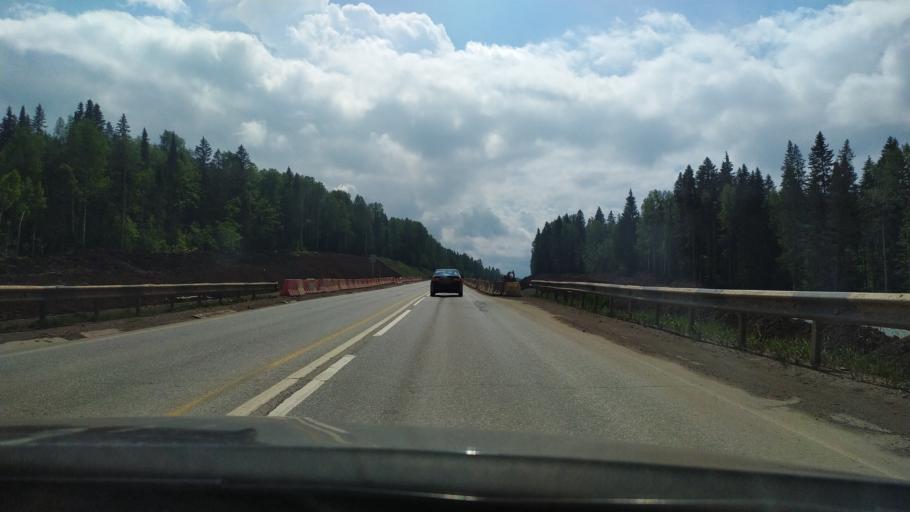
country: RU
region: Perm
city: Novyye Lyady
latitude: 58.0852
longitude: 56.4294
